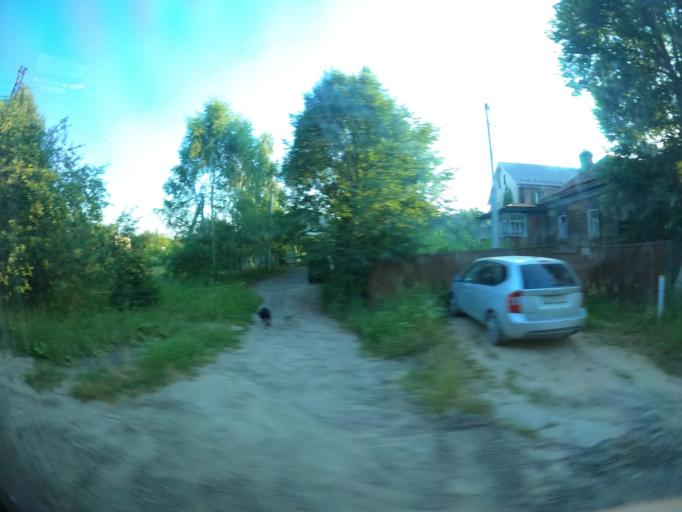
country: RU
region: Moskovskaya
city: Serpukhov
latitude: 54.9456
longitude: 37.3482
